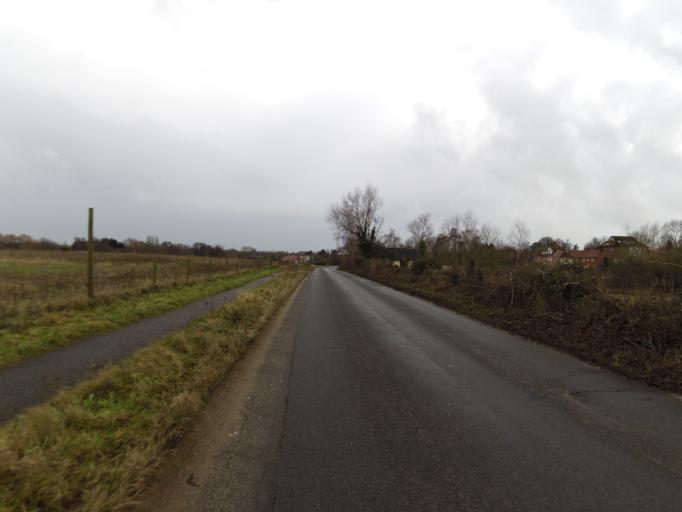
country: GB
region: England
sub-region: Suffolk
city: Needham Market
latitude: 52.1585
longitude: 1.0543
